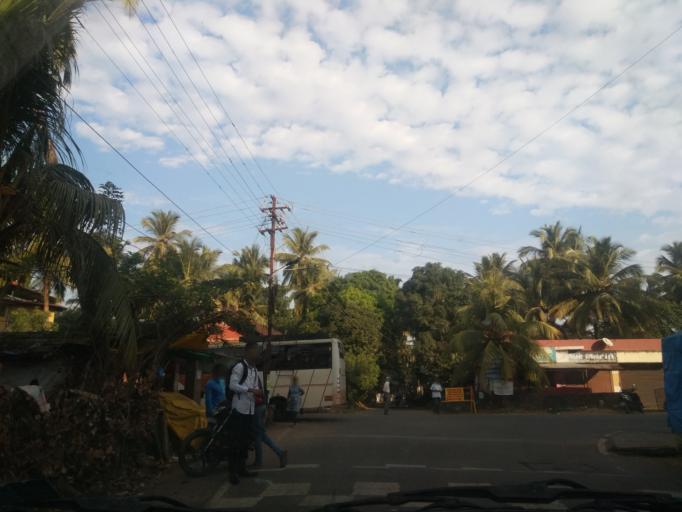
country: IN
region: Goa
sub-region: South Goa
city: Madgaon
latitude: 15.2531
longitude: 73.9561
